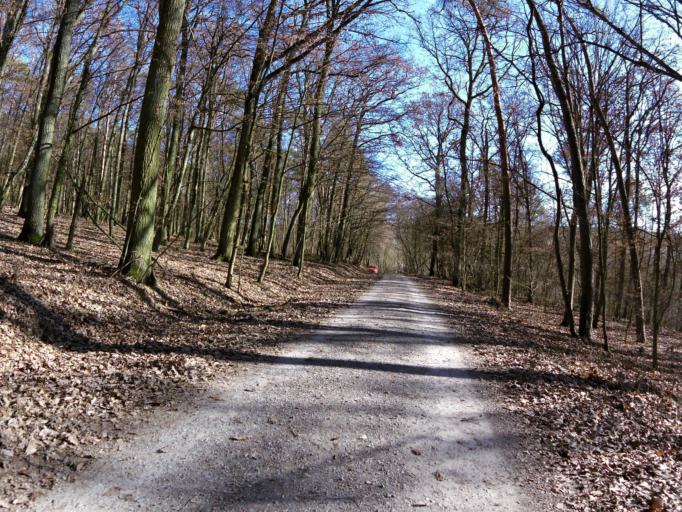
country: DE
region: Bavaria
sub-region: Regierungsbezirk Unterfranken
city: Estenfeld
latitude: 49.8505
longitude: 9.9866
